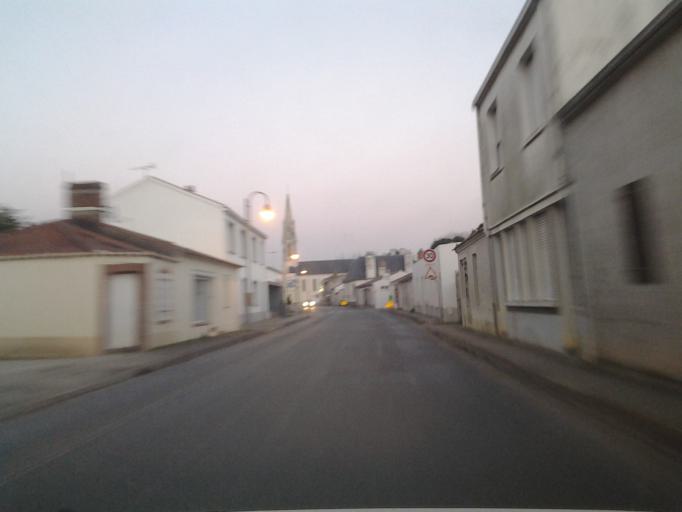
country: FR
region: Pays de la Loire
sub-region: Departement de la Vendee
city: Saint-Gervais
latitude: 46.9026
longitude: -2.0037
